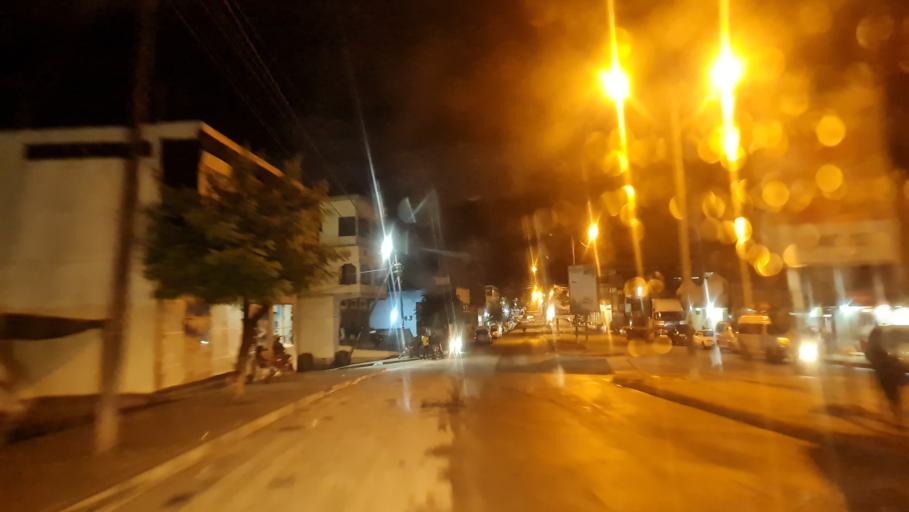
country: MZ
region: Nampula
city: Nampula
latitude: -15.1149
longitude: 39.2810
